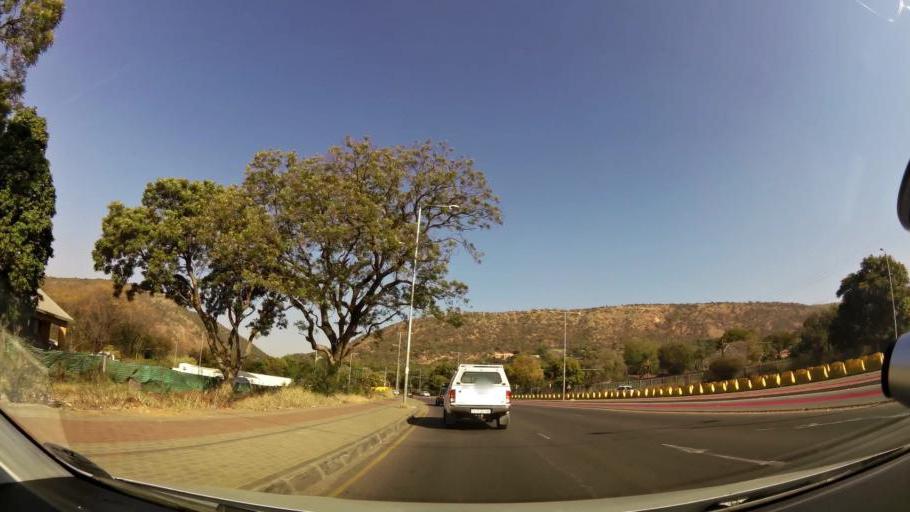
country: ZA
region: Gauteng
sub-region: City of Tshwane Metropolitan Municipality
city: Pretoria
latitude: -25.6832
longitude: 28.1836
